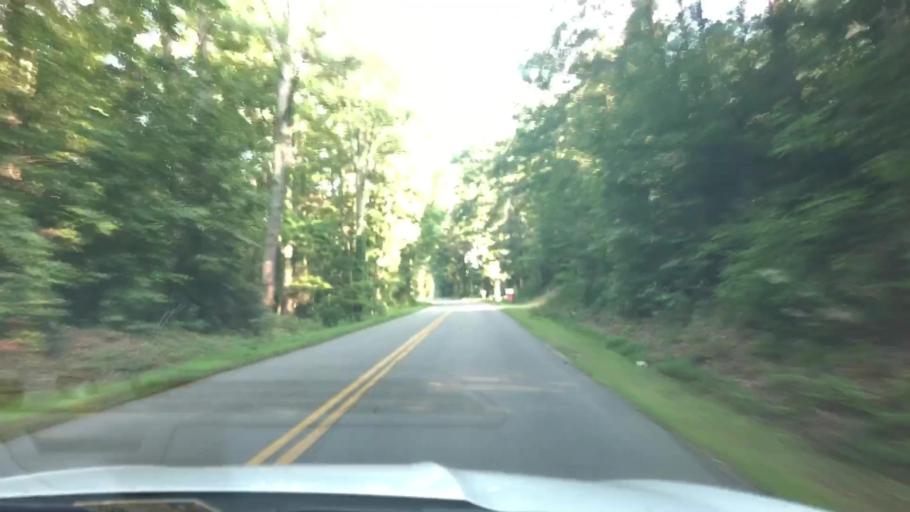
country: US
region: Virginia
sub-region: Middlesex County
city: Saluda
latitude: 37.6237
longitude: -76.7037
